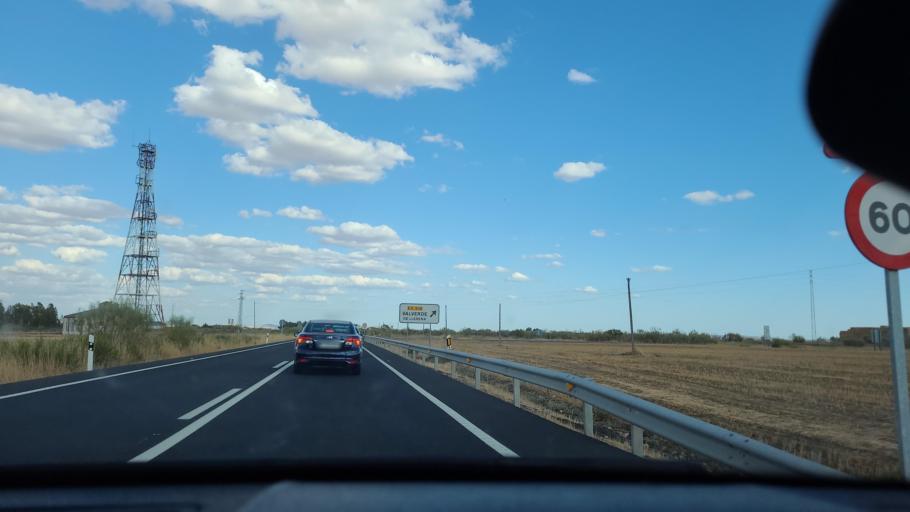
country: ES
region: Extremadura
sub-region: Provincia de Badajoz
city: Azuaga
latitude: 38.2601
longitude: -5.7220
